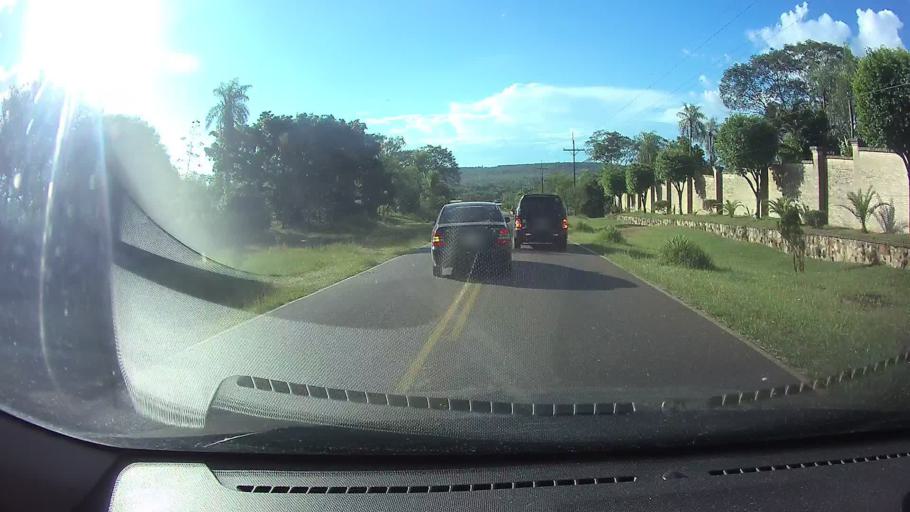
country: PY
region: Cordillera
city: Altos
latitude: -25.2679
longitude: -57.2417
